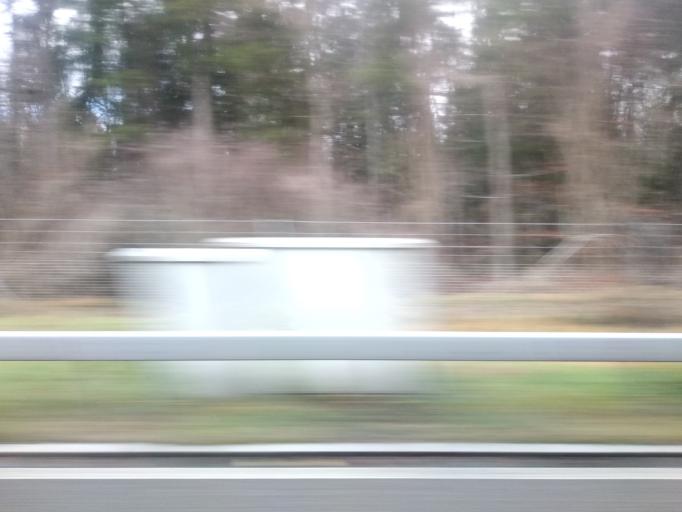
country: CH
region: Saint Gallen
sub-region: Wahlkreis Wil
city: Wil
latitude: 47.4568
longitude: 9.0714
